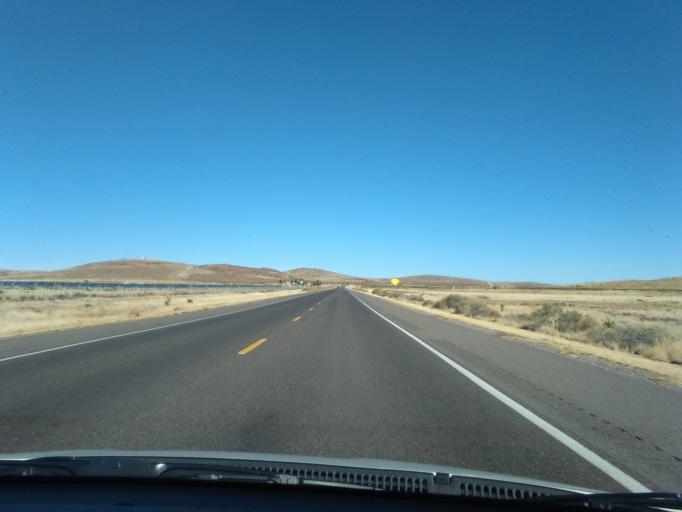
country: US
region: New Mexico
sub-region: Dona Ana County
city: Hatch
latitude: 32.5691
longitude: -107.4593
